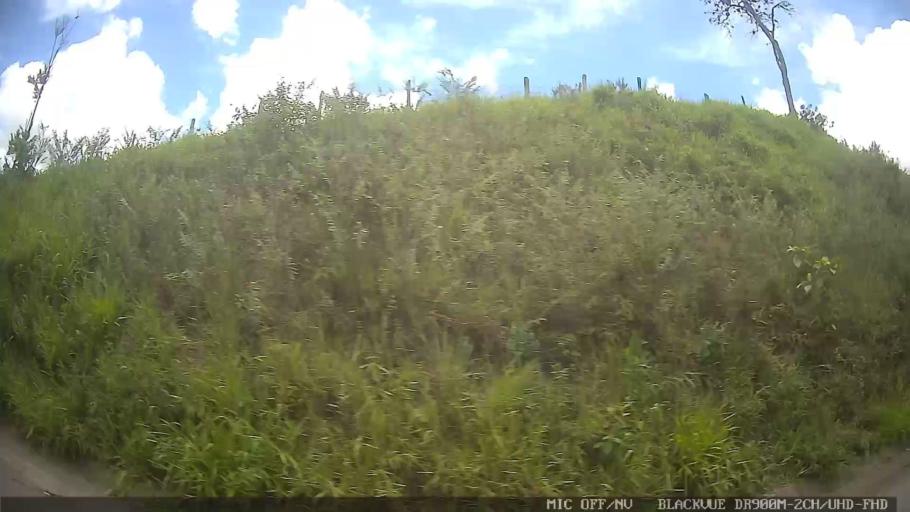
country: BR
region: Sao Paulo
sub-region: Amparo
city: Amparo
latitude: -22.7654
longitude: -46.7472
